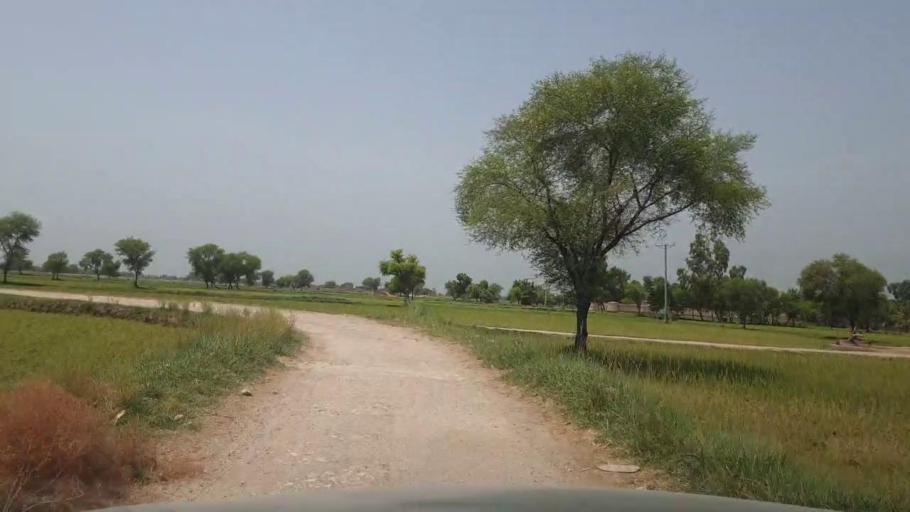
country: PK
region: Sindh
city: Garhi Yasin
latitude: 27.9221
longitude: 68.3707
